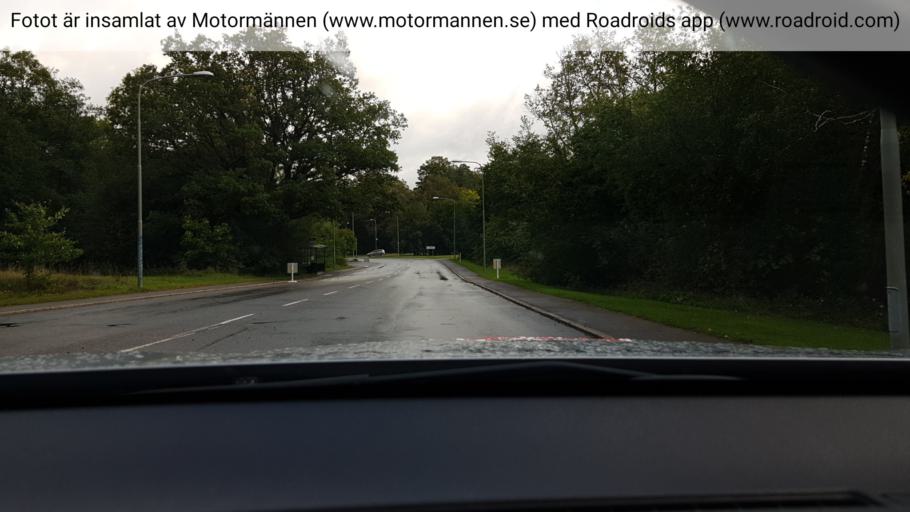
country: SE
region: Stockholm
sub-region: Stockholms Kommun
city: Arsta
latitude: 59.2500
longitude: 18.1052
